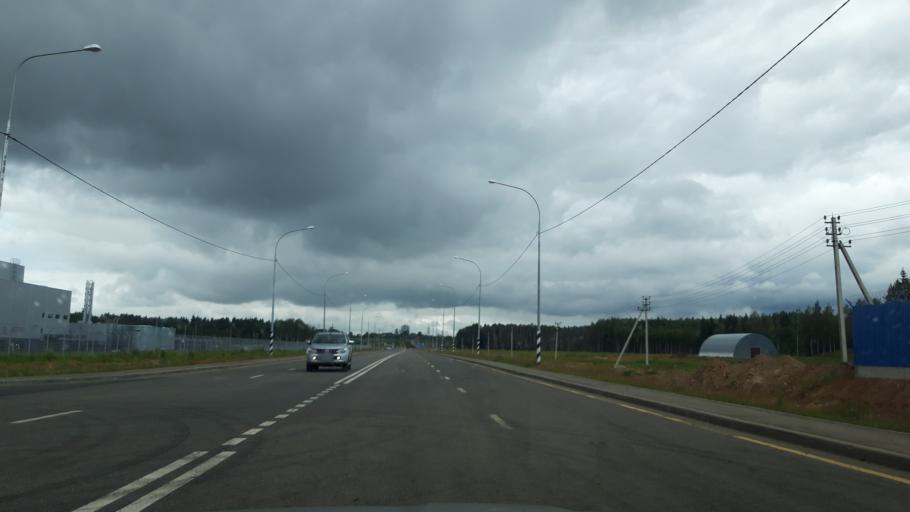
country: RU
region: Moskovskaya
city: Lozhki
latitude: 56.0834
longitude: 37.0866
